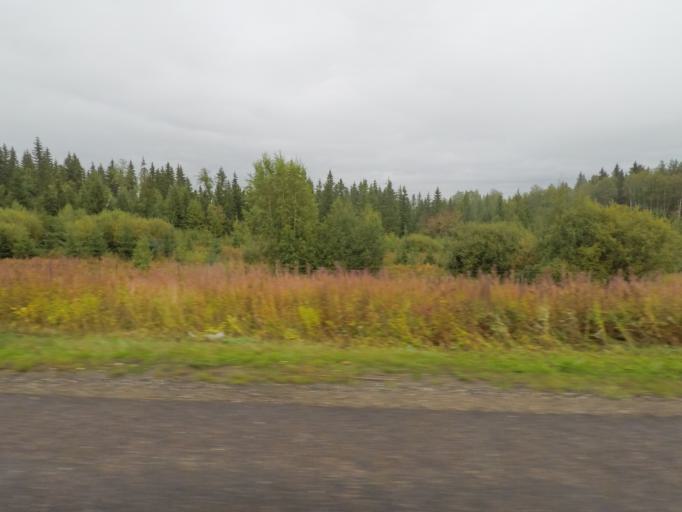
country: FI
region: Northern Savo
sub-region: Varkaus
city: Varkaus
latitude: 62.2520
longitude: 27.8786
